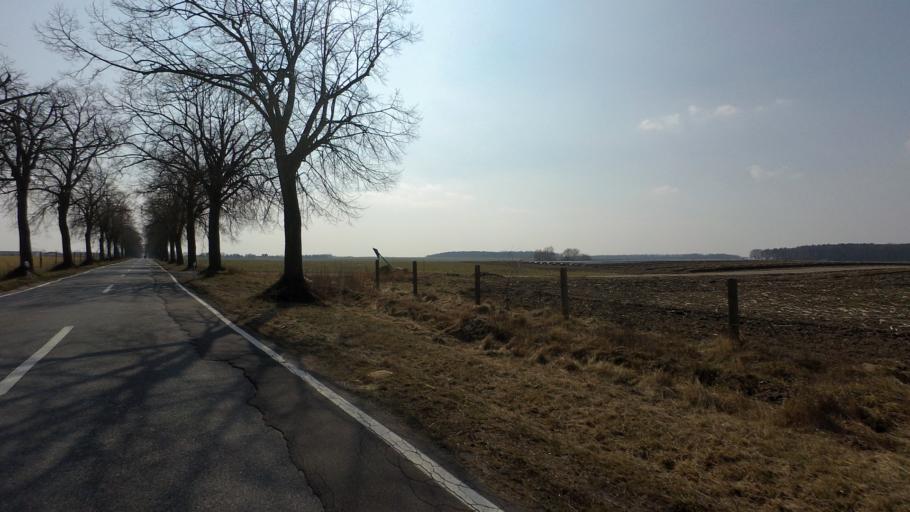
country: DE
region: Brandenburg
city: Gross Kreutz
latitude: 52.4273
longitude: 12.7875
